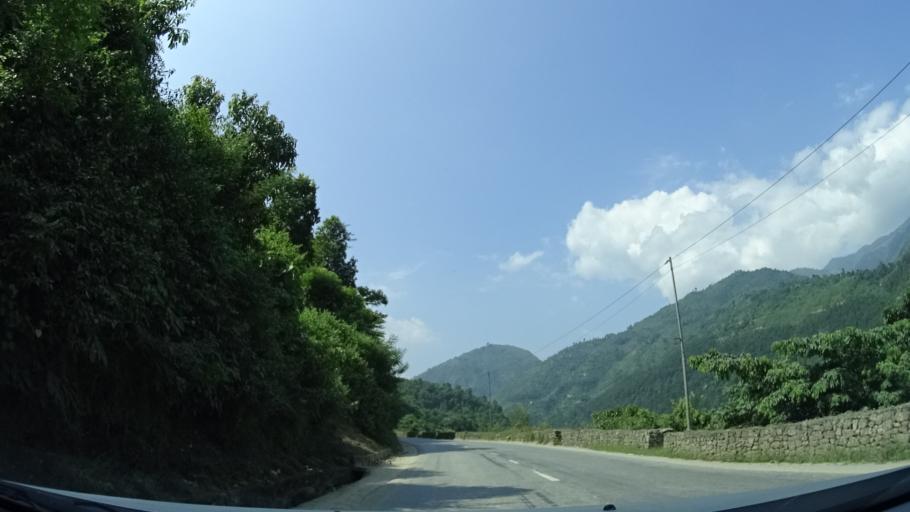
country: NP
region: Central Region
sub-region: Narayani Zone
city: Bharatpur
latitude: 27.8001
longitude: 84.7100
